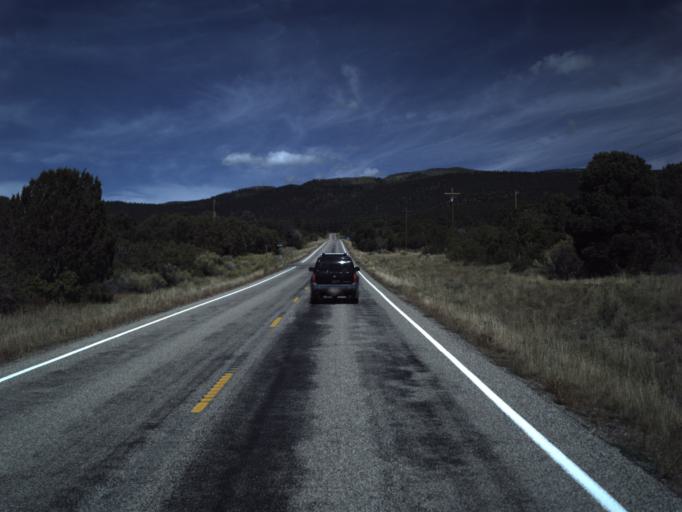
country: US
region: Utah
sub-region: Wayne County
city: Loa
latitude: 37.9755
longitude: -111.4311
